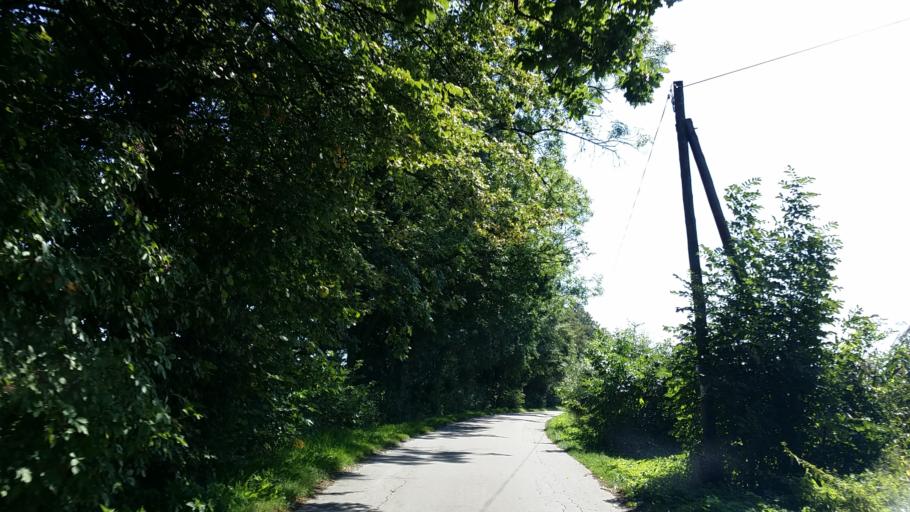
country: PL
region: Lesser Poland Voivodeship
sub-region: Powiat oswiecimski
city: Przeciszow
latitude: 50.0140
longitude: 19.4043
